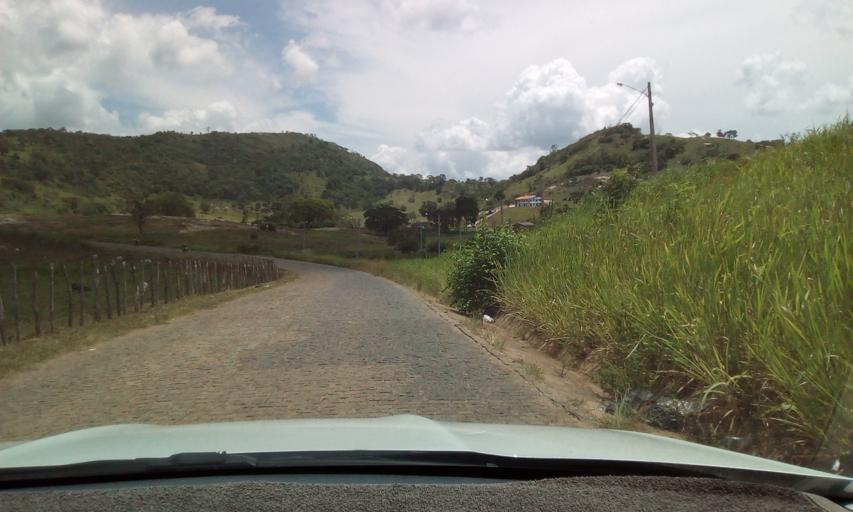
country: BR
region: Pernambuco
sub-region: Bonito
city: Bonito
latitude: -8.4844
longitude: -35.7307
